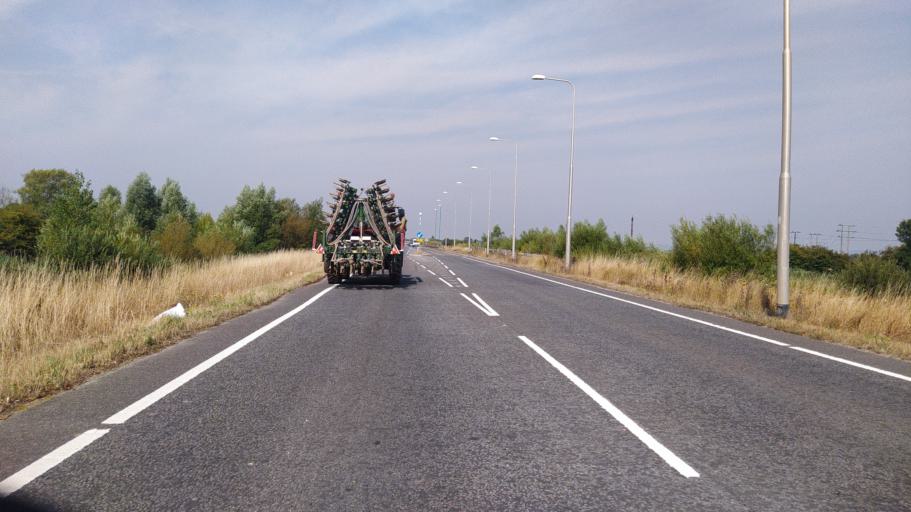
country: GB
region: England
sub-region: West Sussex
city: Bognor Regis
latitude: 50.8061
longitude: -0.6822
